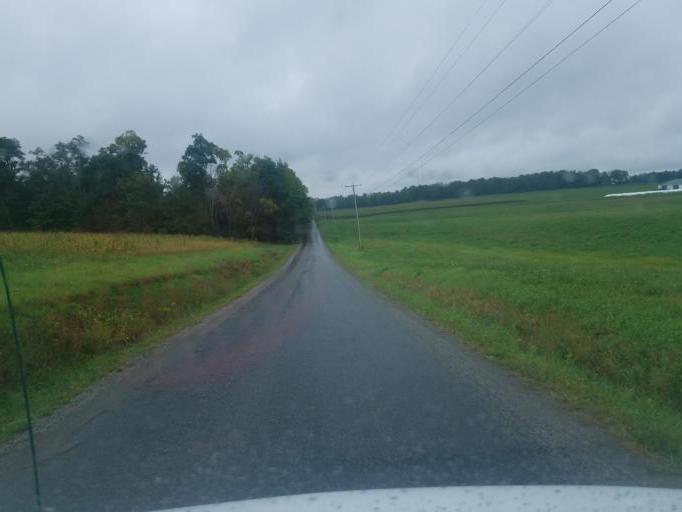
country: US
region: Ohio
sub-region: Wayne County
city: West Salem
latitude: 40.9294
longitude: -82.1378
